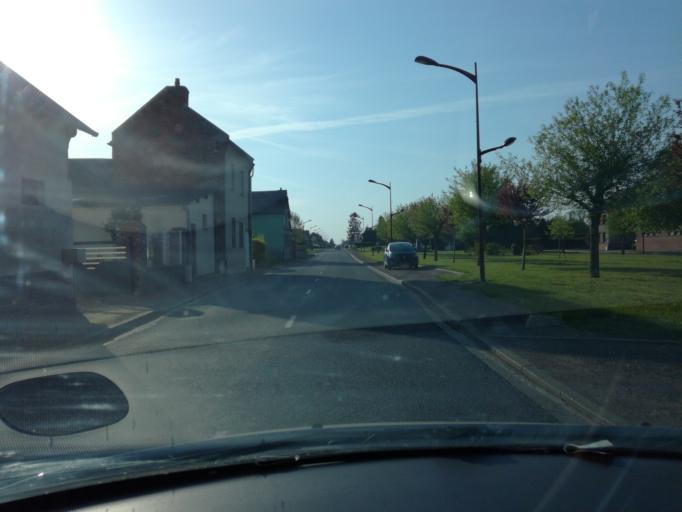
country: FR
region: Picardie
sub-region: Departement de la Somme
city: Hornoy-le-Bourg
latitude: 49.8245
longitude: 1.9467
